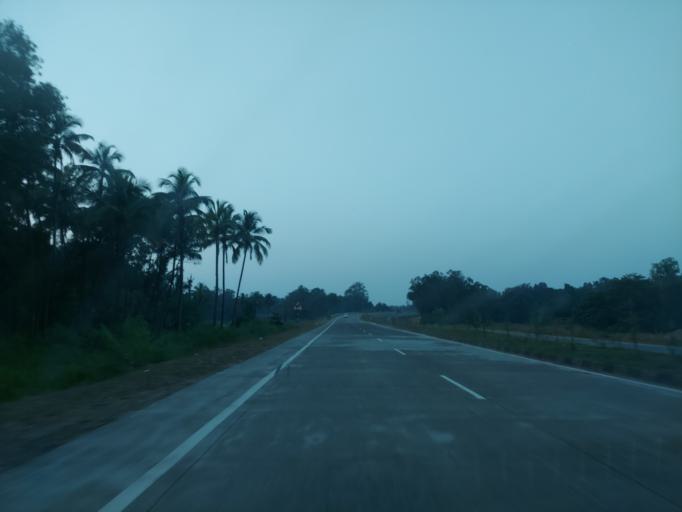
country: IN
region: Maharashtra
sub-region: Sindhudurg
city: Kudal
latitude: 16.0905
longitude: 73.7073
